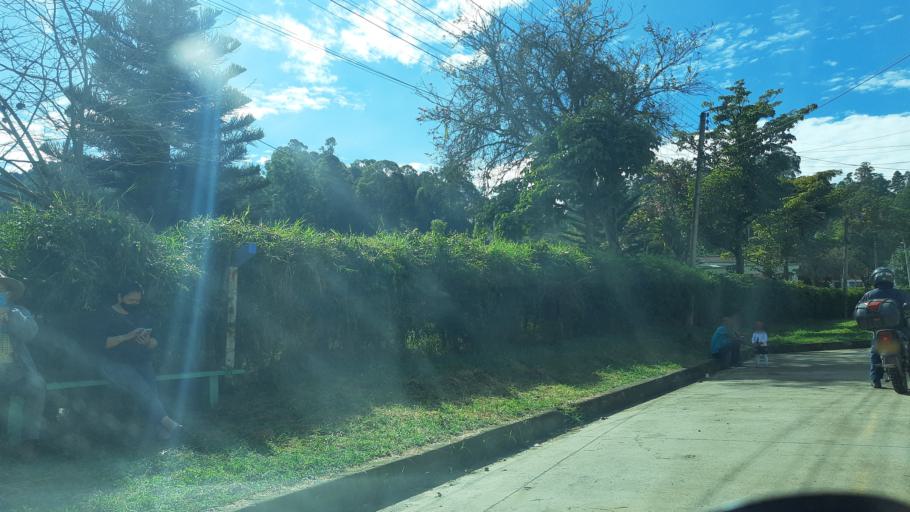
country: CO
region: Boyaca
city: Garagoa
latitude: 5.0785
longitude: -73.3624
